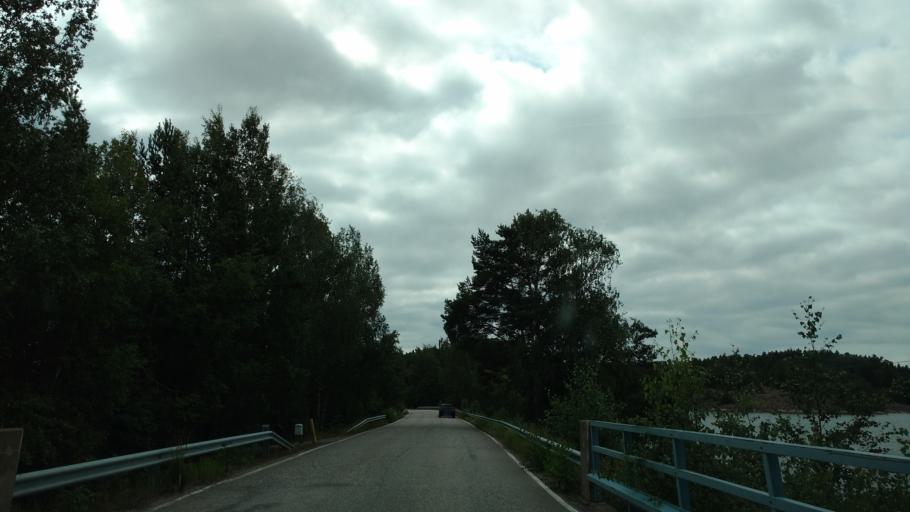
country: FI
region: Varsinais-Suomi
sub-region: Aboland-Turunmaa
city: Dragsfjaerd
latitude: 59.9984
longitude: 22.4530
